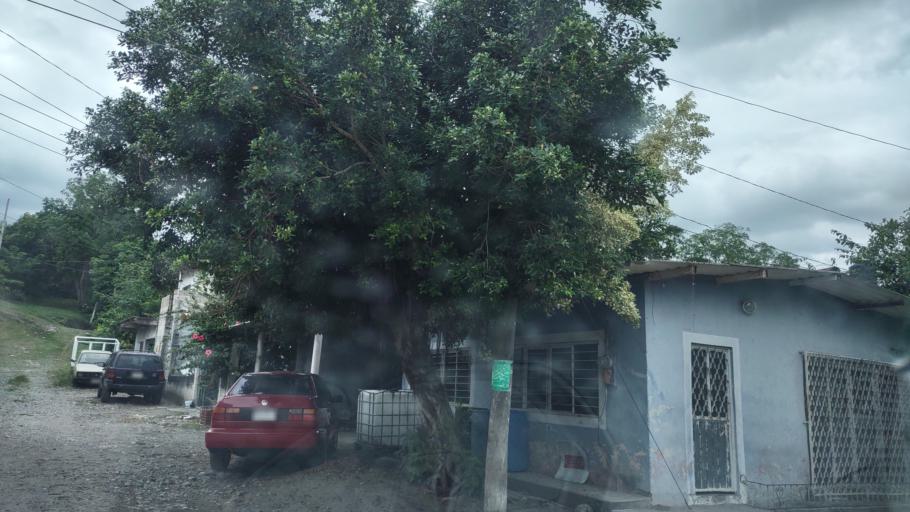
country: MX
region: Veracruz
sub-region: Martinez de la Torre
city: El Progreso
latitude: 20.0898
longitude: -97.0207
